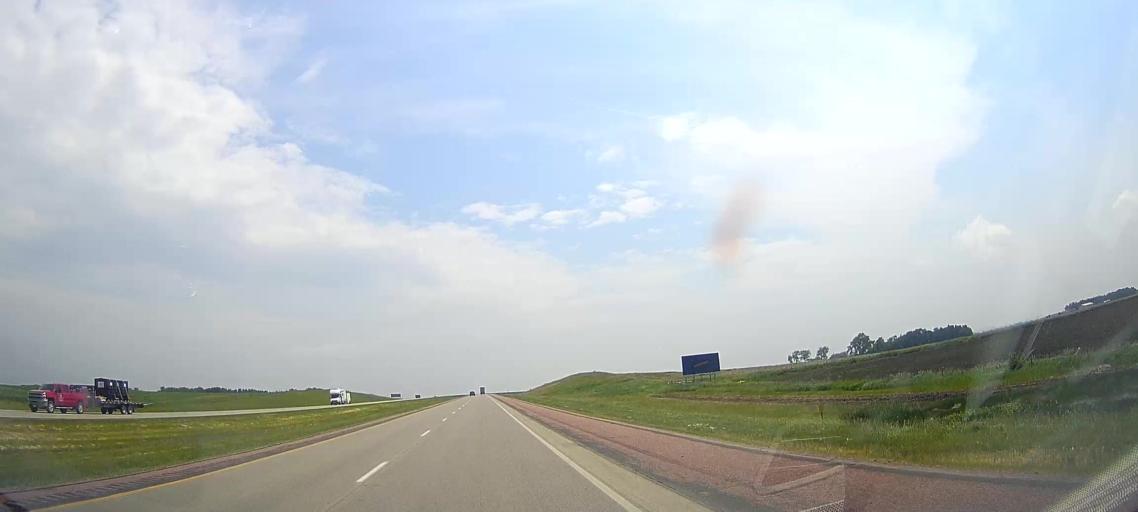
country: US
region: South Dakota
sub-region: Union County
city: Beresford
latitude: 43.0479
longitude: -96.7958
